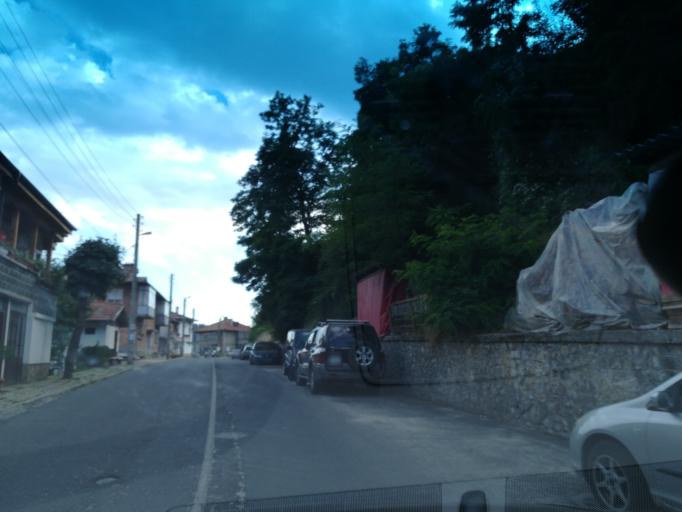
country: BG
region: Smolyan
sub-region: Obshtina Smolyan
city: Smolyan
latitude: 41.6571
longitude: 24.7729
